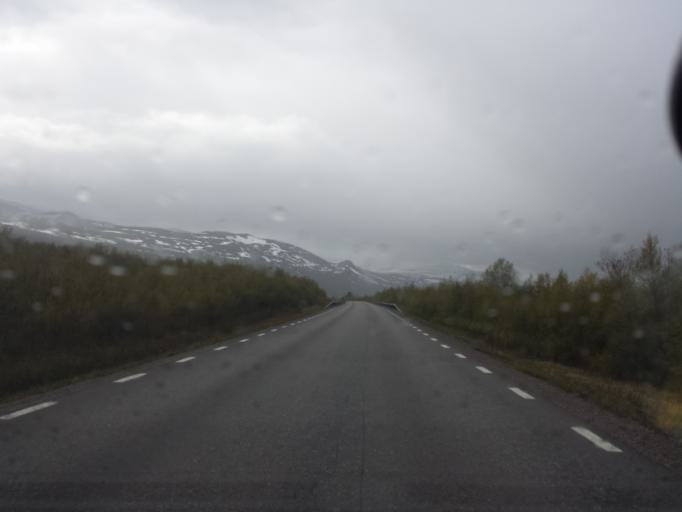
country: SE
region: Norrbotten
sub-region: Kiruna Kommun
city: Kiruna
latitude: 68.2326
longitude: 19.6105
